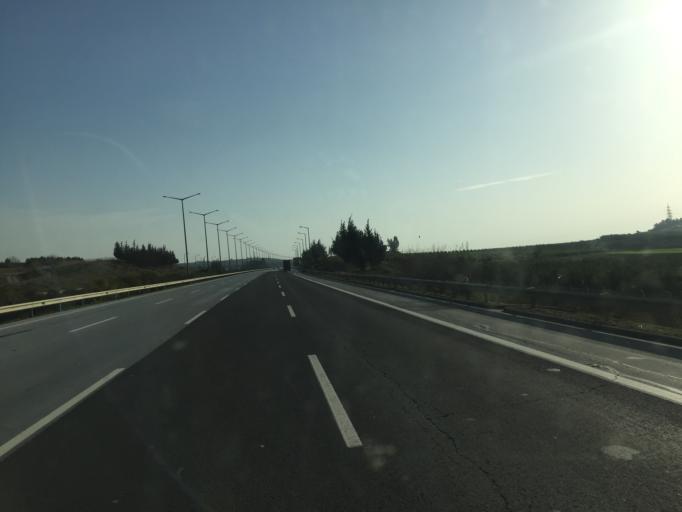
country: TR
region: Mersin
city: Yenice
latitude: 37.0233
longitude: 35.0556
